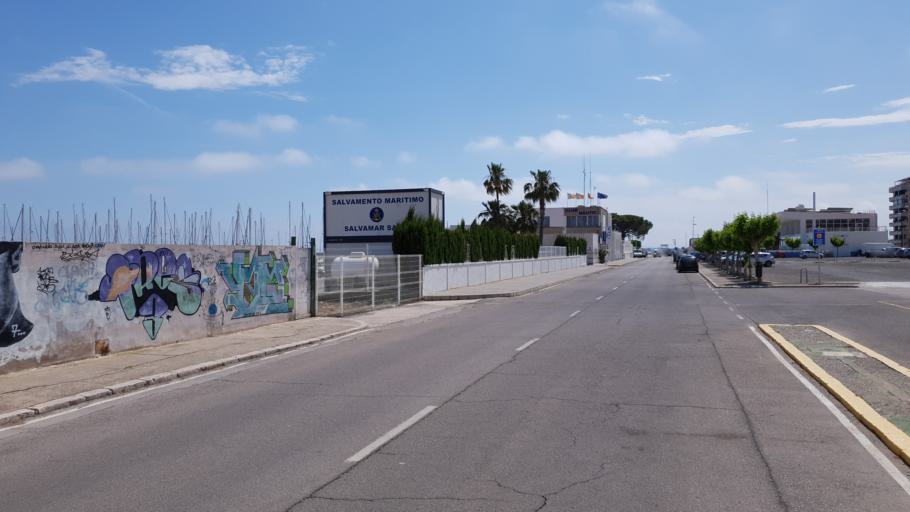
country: ES
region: Valencia
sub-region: Provincia de Castello
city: Burriana
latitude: 39.8642
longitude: -0.0733
